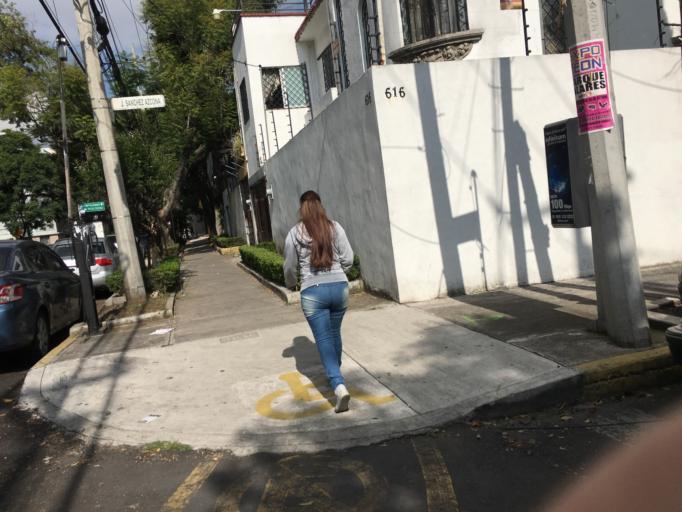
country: MX
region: Mexico City
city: Colonia del Valle
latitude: 19.3752
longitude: -99.1646
